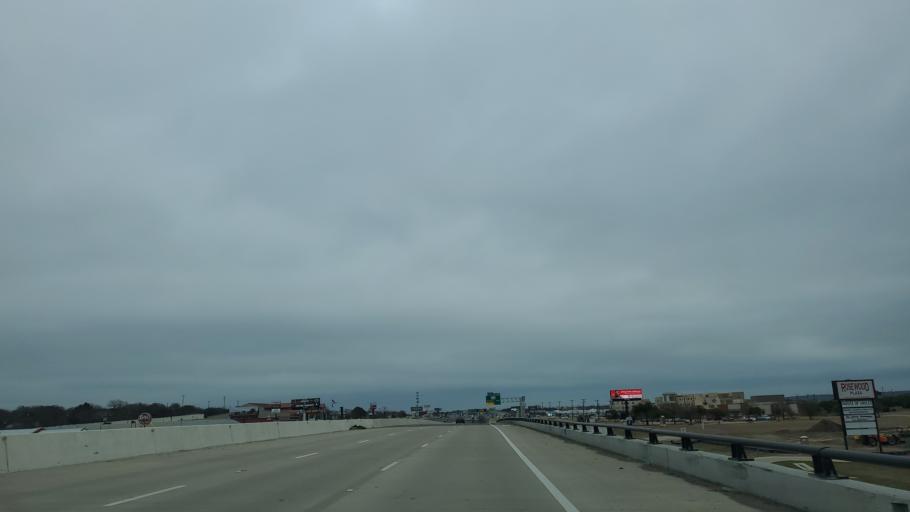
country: US
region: Texas
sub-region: Bell County
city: Harker Heights
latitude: 31.0760
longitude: -97.6885
